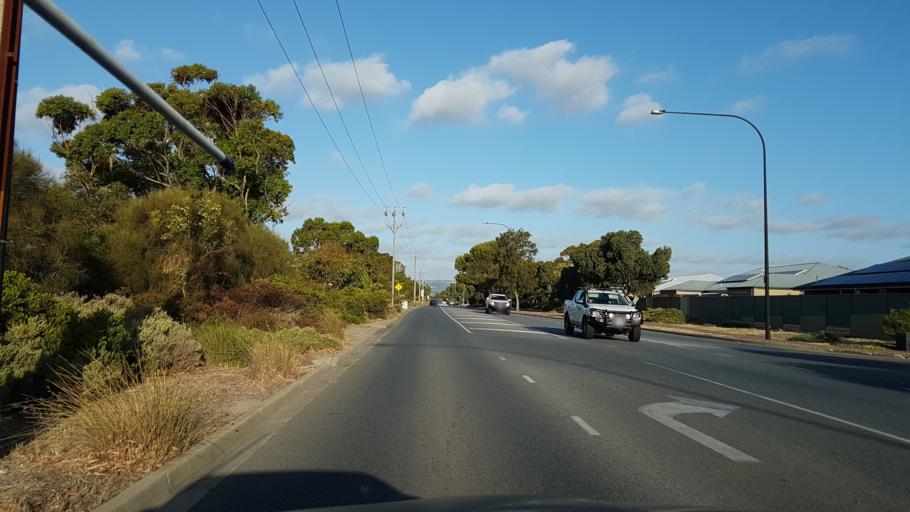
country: AU
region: South Australia
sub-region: Onkaparinga
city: Port Willunga
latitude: -35.2787
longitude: 138.4657
